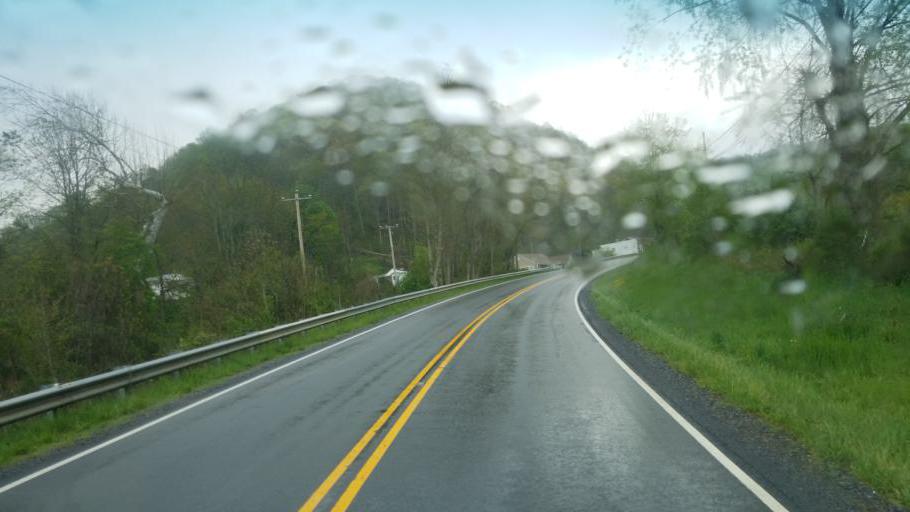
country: US
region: Virginia
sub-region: Smyth County
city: Marion
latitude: 36.8236
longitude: -81.4756
